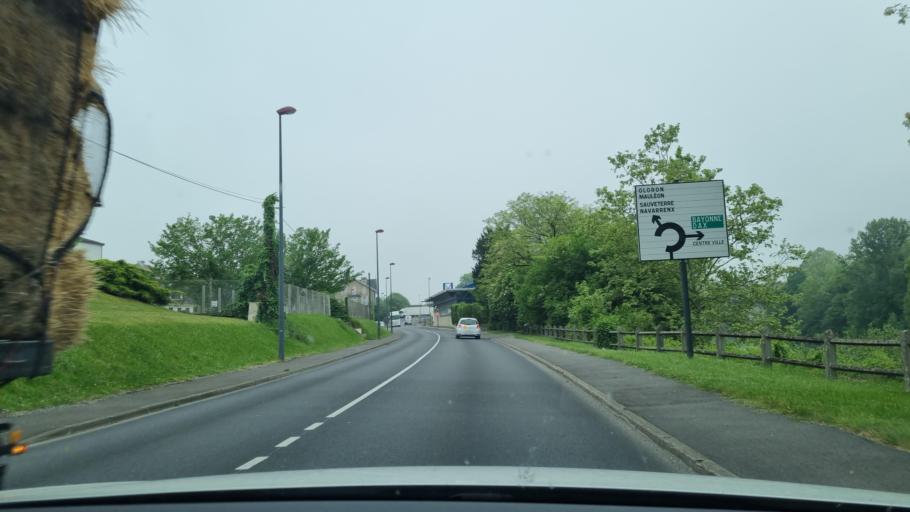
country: FR
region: Aquitaine
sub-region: Departement des Pyrenees-Atlantiques
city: Orthez
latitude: 43.4832
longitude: -0.7721
